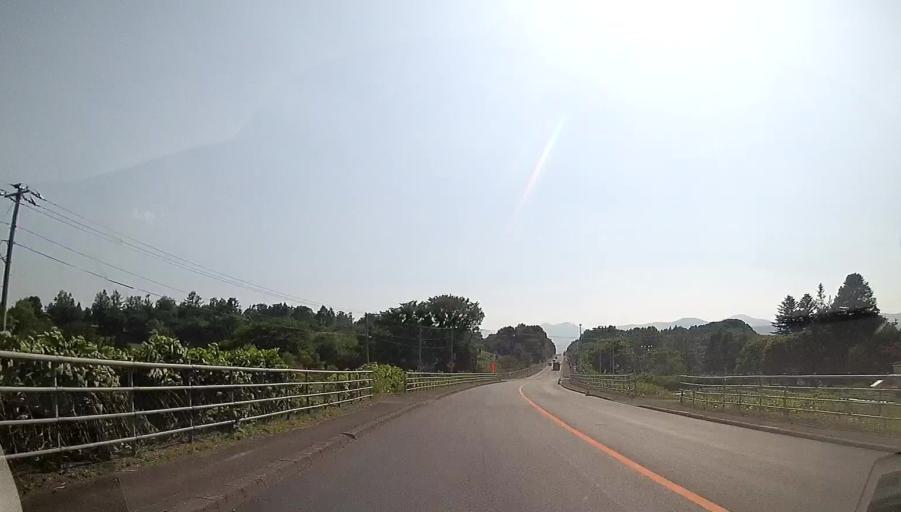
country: JP
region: Hokkaido
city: Otofuke
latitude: 43.0061
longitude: 142.8768
